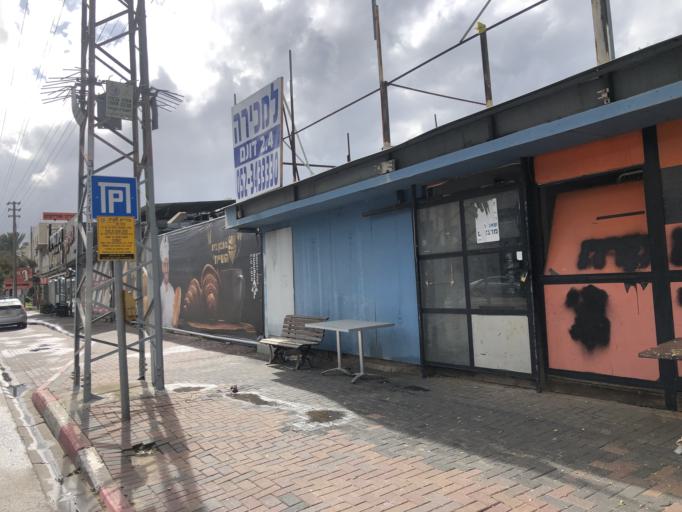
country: IL
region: Central District
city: Bet Yizhaq
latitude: 32.3226
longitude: 34.8744
